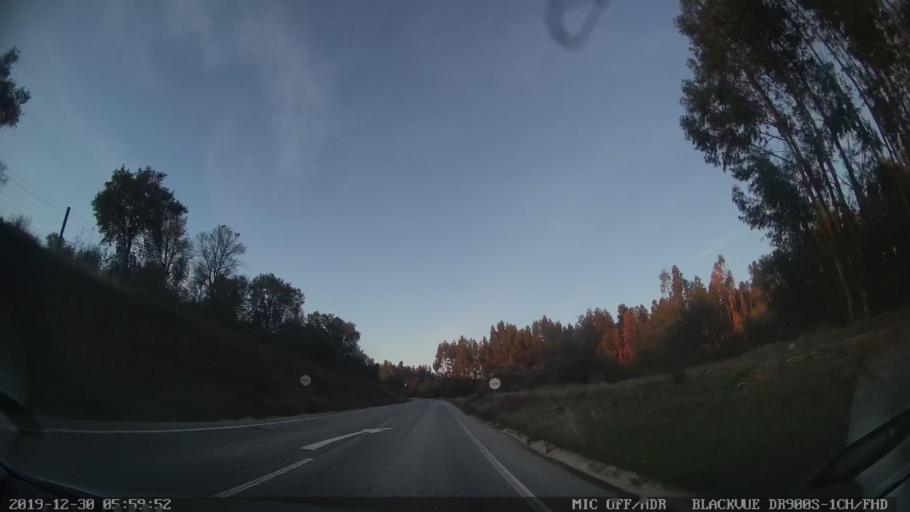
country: PT
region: Castelo Branco
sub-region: Idanha-A-Nova
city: Idanha-a-Nova
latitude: 40.0474
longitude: -7.2437
